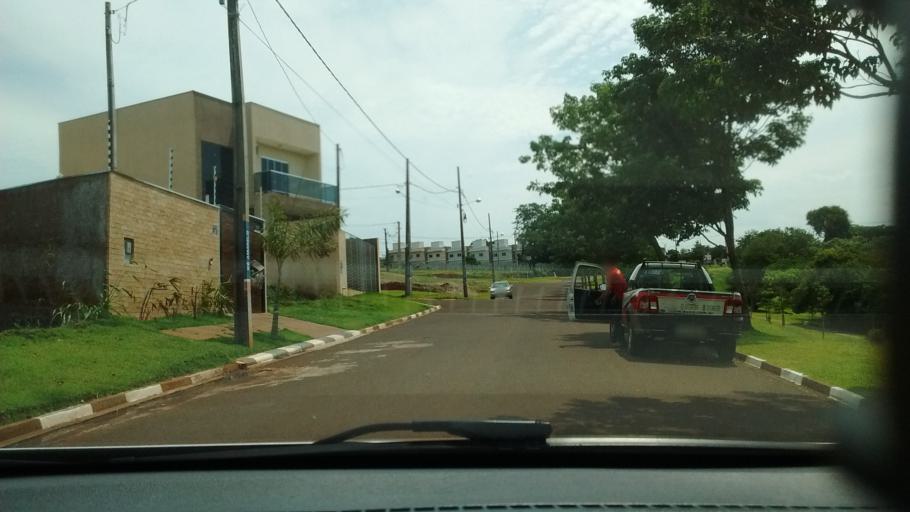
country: BR
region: Parana
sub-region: Corbelia
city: Corbelia
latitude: -24.5490
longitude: -52.9789
